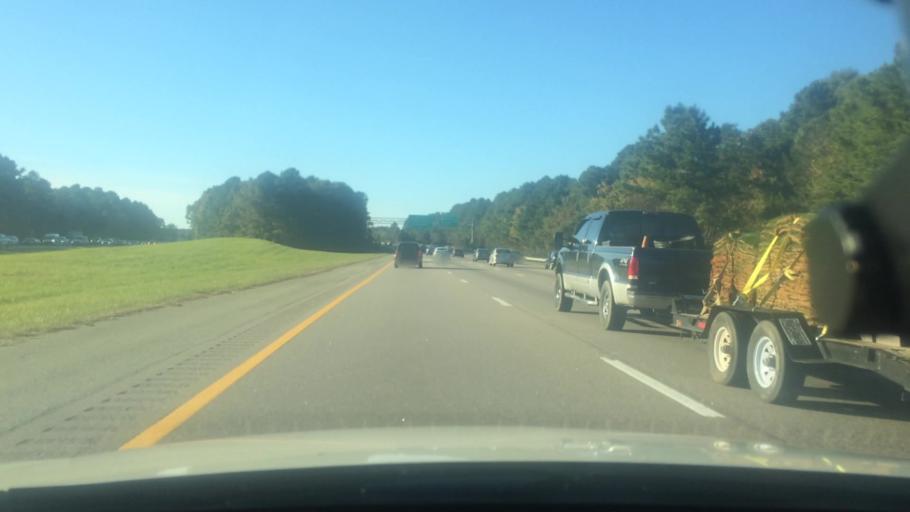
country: US
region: North Carolina
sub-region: Wake County
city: Morrisville
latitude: 35.8967
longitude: -78.8649
